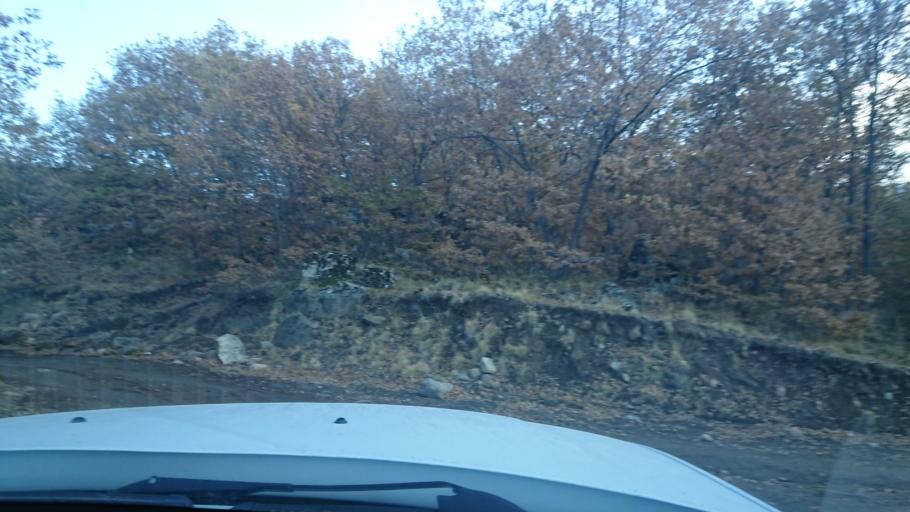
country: TR
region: Aksaray
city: Taspinar
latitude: 38.1651
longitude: 34.2077
